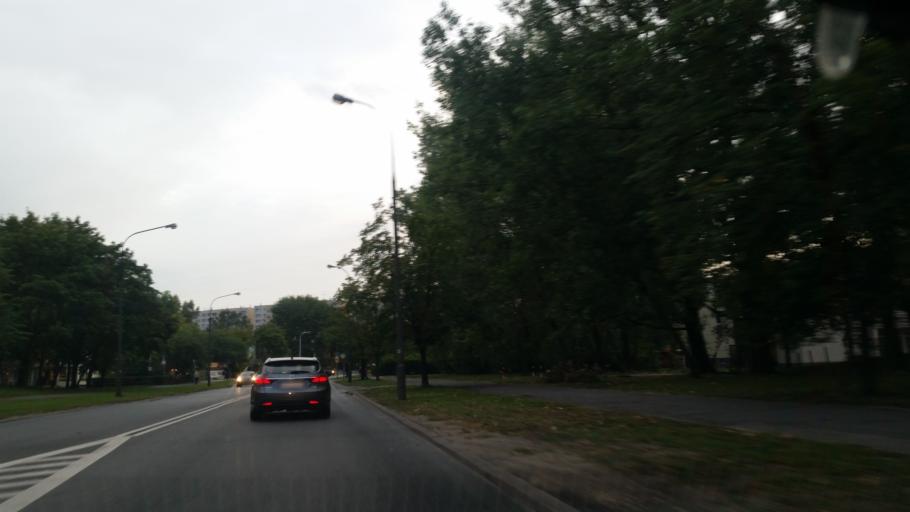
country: PL
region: Masovian Voivodeship
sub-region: Warszawa
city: Mokotow
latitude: 52.1792
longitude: 21.0518
